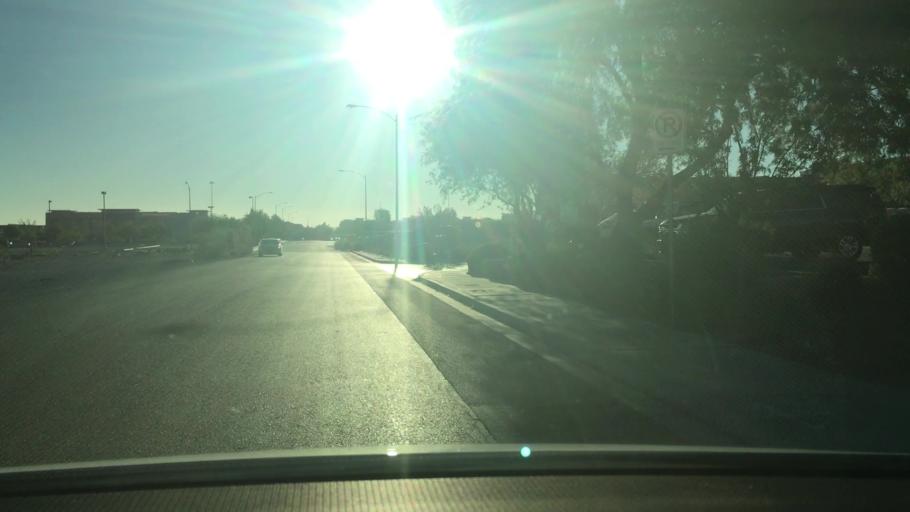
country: US
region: Nevada
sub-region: Clark County
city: Summerlin South
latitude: 36.0739
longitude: -115.2945
